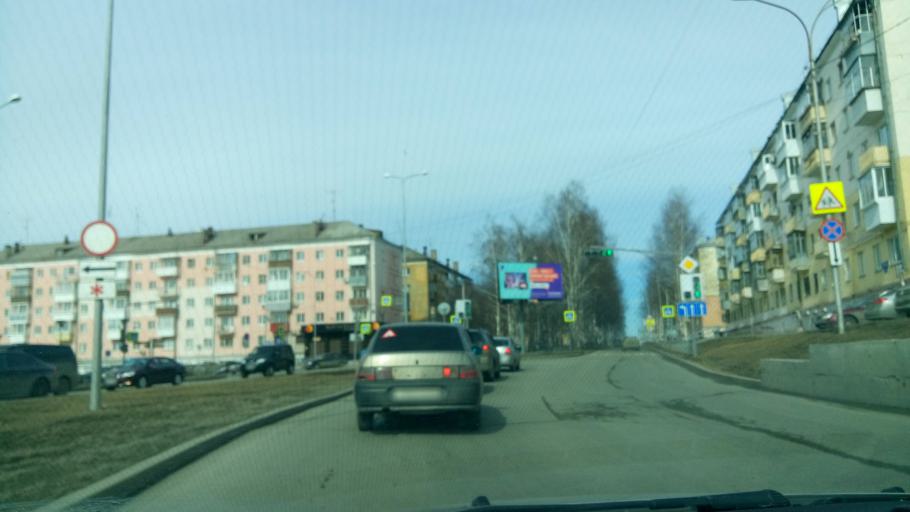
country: RU
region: Sverdlovsk
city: Nizhniy Tagil
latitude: 57.9055
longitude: 59.9851
